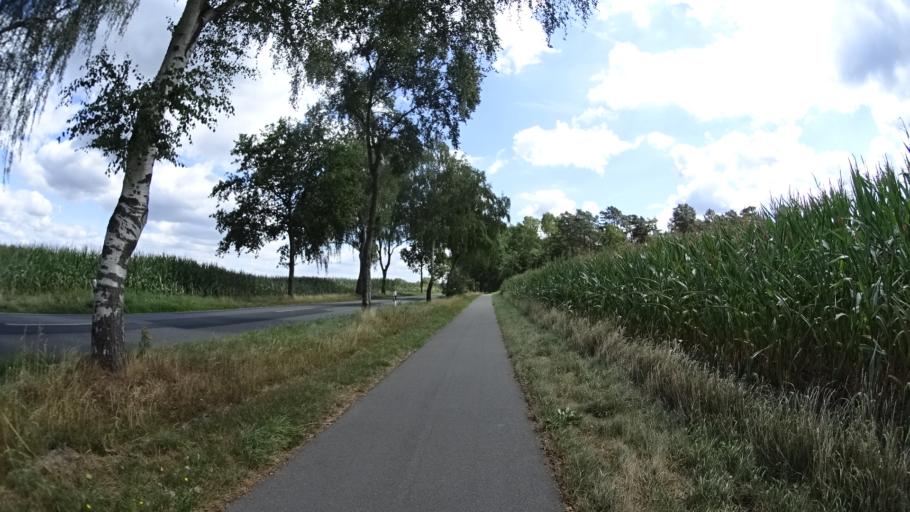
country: DE
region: Lower Saxony
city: Undeloh
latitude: 53.2233
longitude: 9.9311
